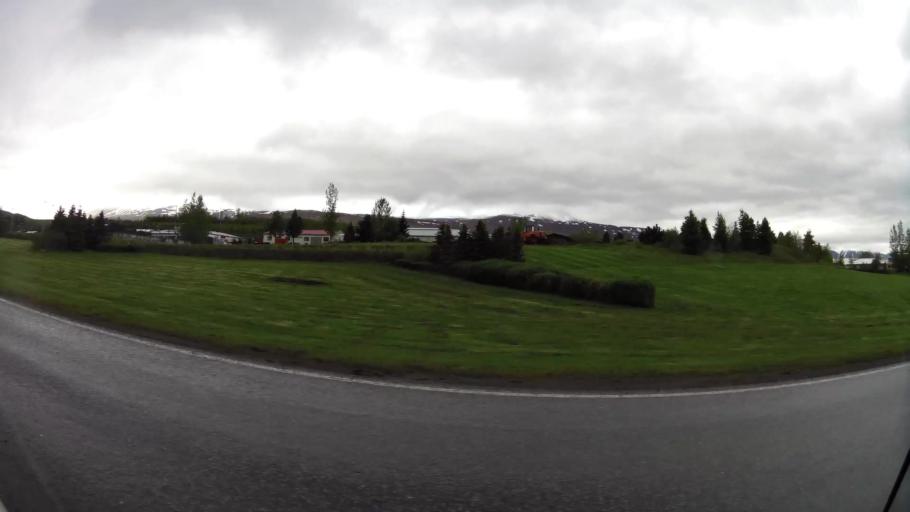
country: IS
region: Northeast
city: Akureyri
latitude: 65.6801
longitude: -18.1318
